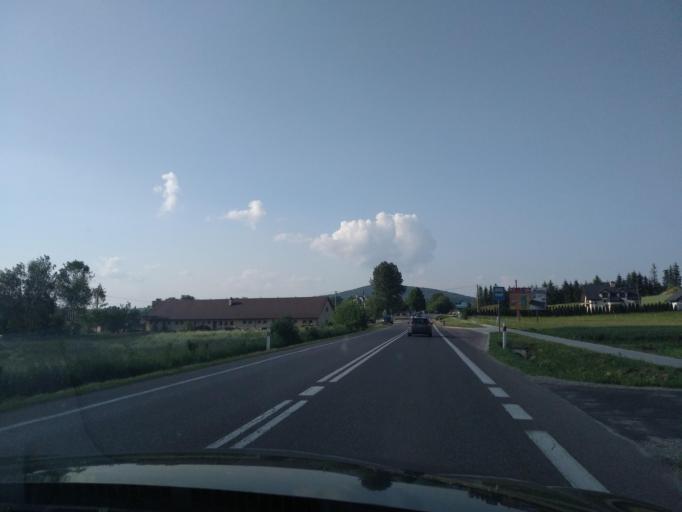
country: PL
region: Subcarpathian Voivodeship
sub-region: Powiat sanocki
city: Strachocina
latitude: 49.5918
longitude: 22.1344
